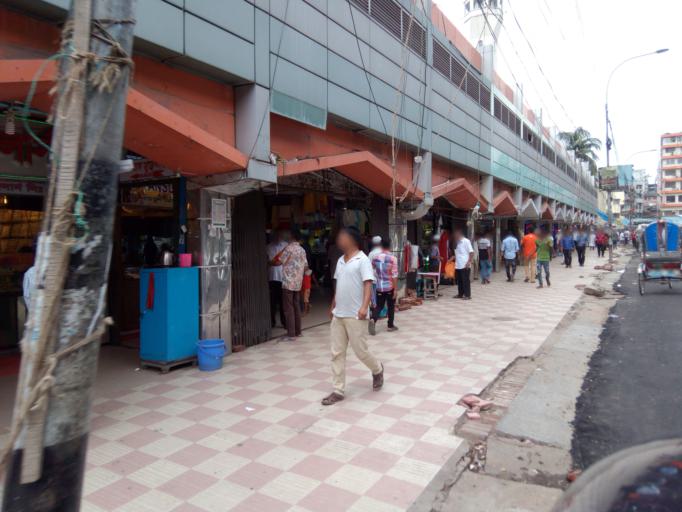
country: BD
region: Dhaka
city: Paltan
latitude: 23.7290
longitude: 90.4117
